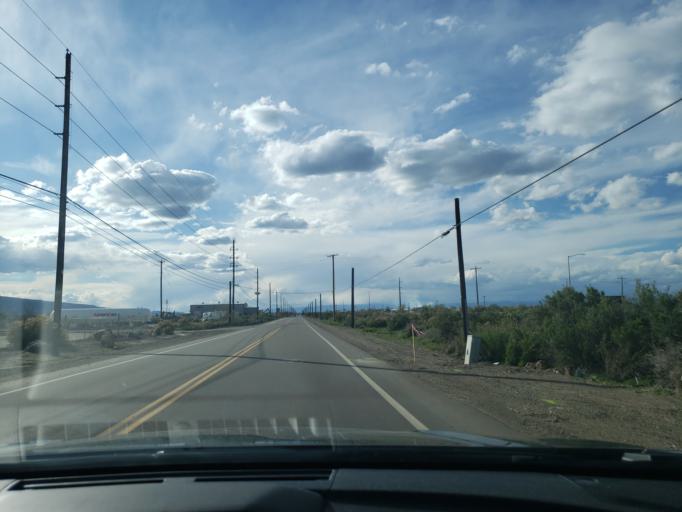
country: US
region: Colorado
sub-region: Mesa County
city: Redlands
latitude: 39.0947
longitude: -108.6164
